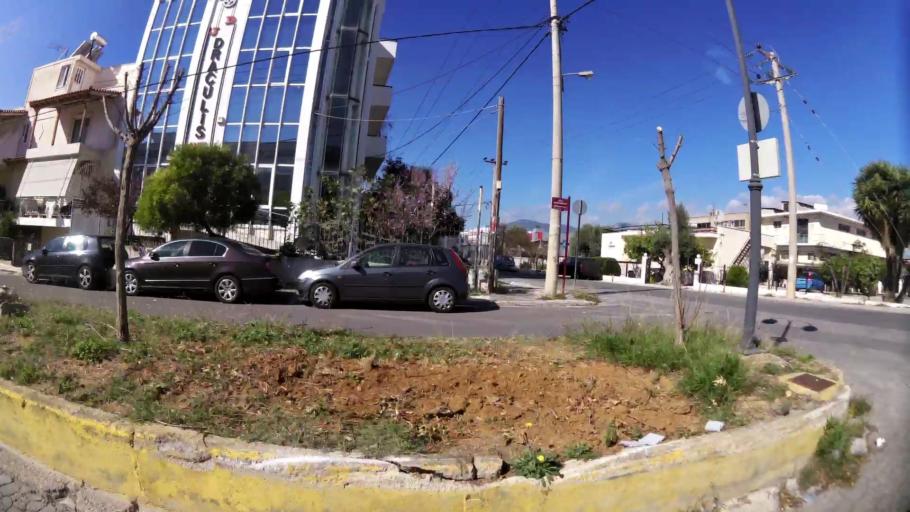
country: GR
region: Attica
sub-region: Nomarchia Athinas
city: Metamorfosi
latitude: 38.0702
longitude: 23.7675
